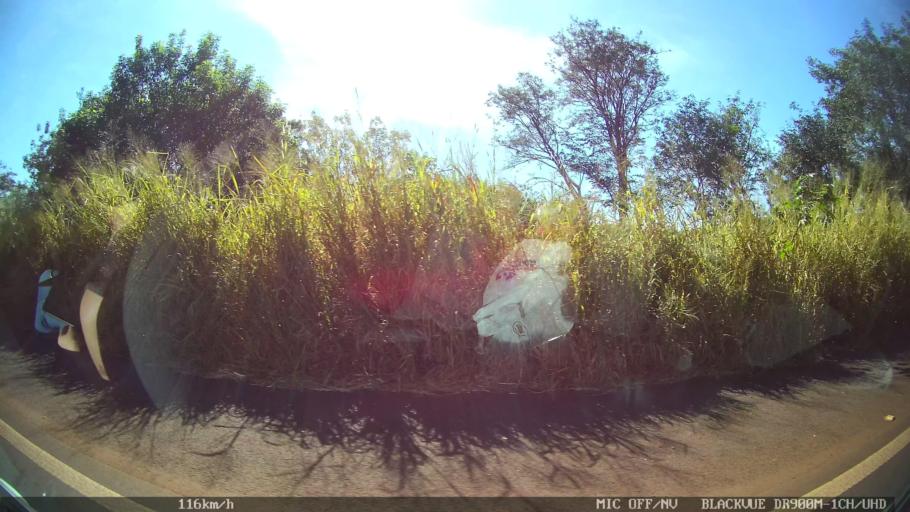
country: BR
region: Sao Paulo
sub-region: Guaira
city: Guaira
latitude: -20.4434
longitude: -48.3267
